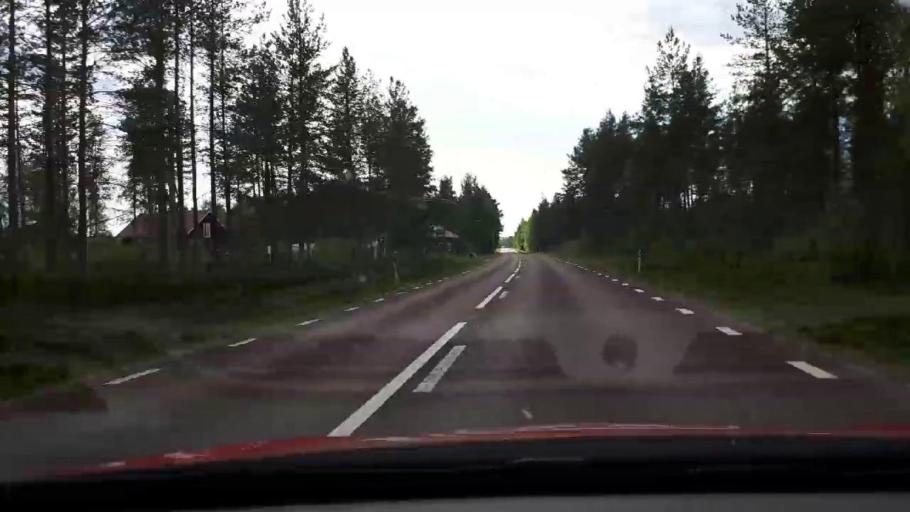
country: SE
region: Jaemtland
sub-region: Harjedalens Kommun
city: Sveg
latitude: 62.1187
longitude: 14.9700
